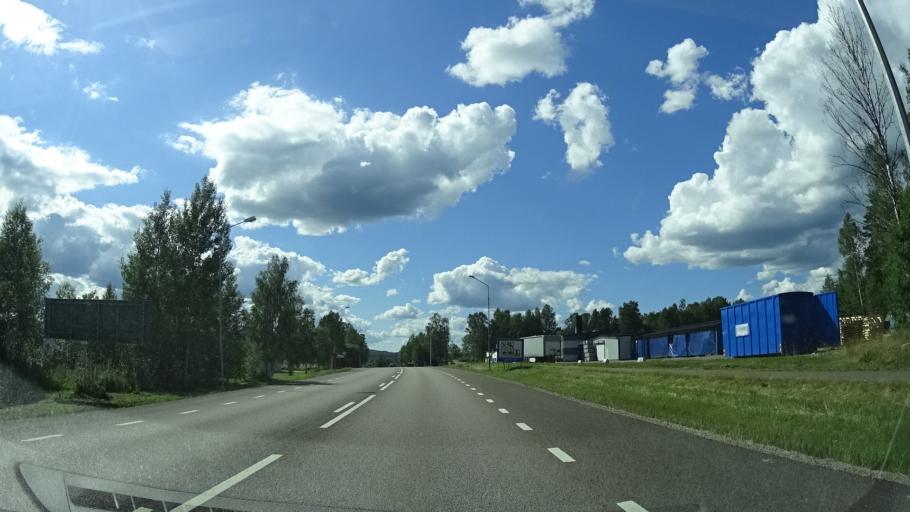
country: SE
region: Vaermland
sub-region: Arjangs Kommun
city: Toecksfors
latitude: 59.5069
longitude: 11.8559
